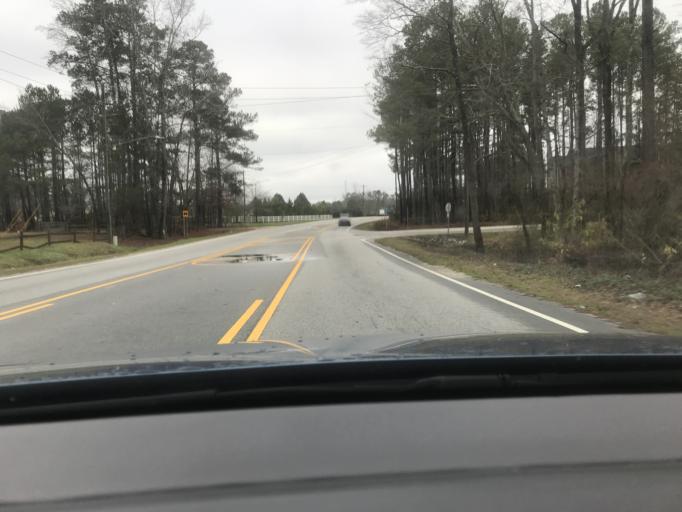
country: US
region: North Carolina
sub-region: Hoke County
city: Rockfish
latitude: 35.0498
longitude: -79.0109
